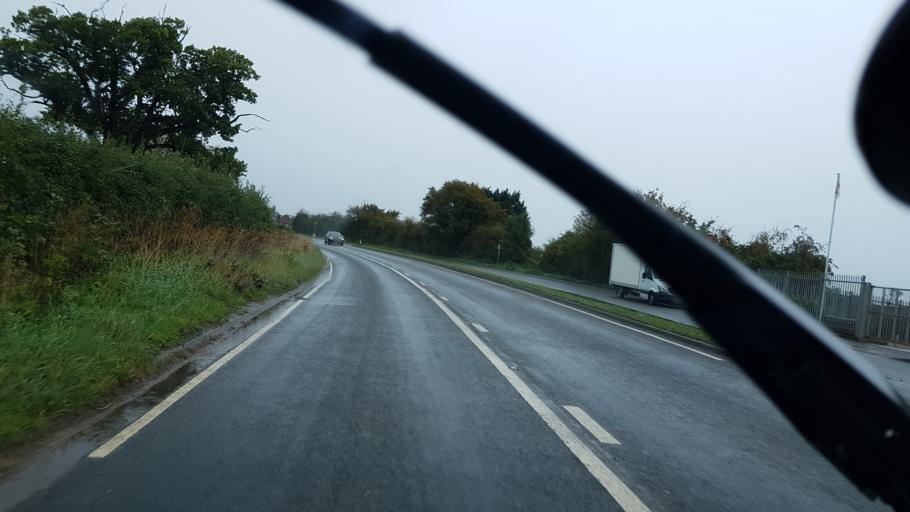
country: GB
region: England
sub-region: Worcestershire
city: Upton upon Severn
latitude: 52.0609
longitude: -2.1933
